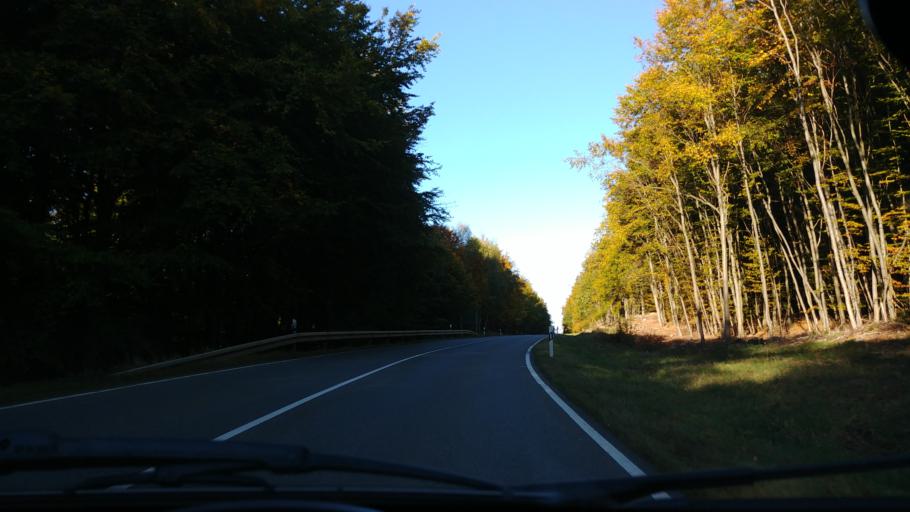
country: DE
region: Rheinland-Pfalz
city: Rettert
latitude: 50.2062
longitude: 7.9431
